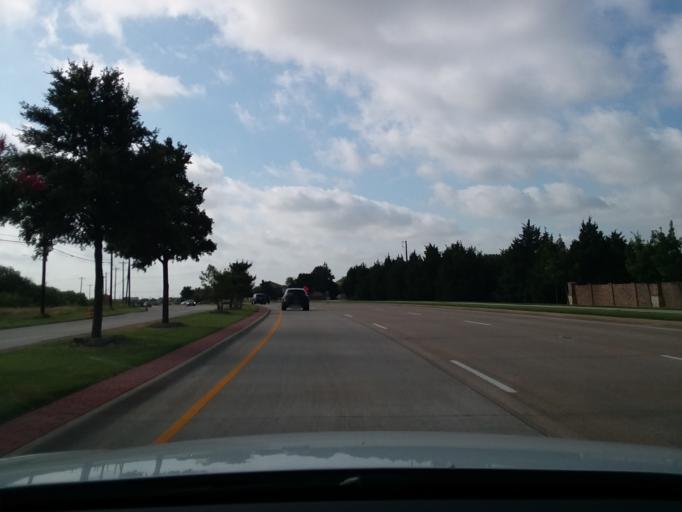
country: US
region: Texas
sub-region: Denton County
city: Flower Mound
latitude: 33.0004
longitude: -97.0692
